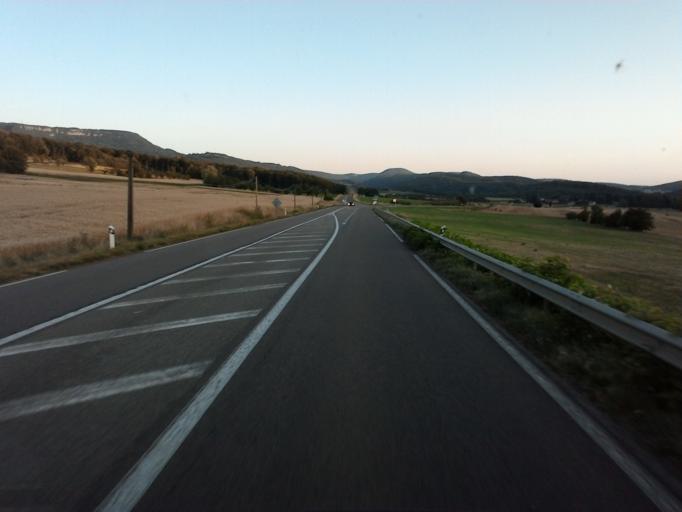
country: FR
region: Franche-Comte
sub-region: Departement du Jura
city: Salins-les-Bains
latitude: 47.0233
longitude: 5.8684
